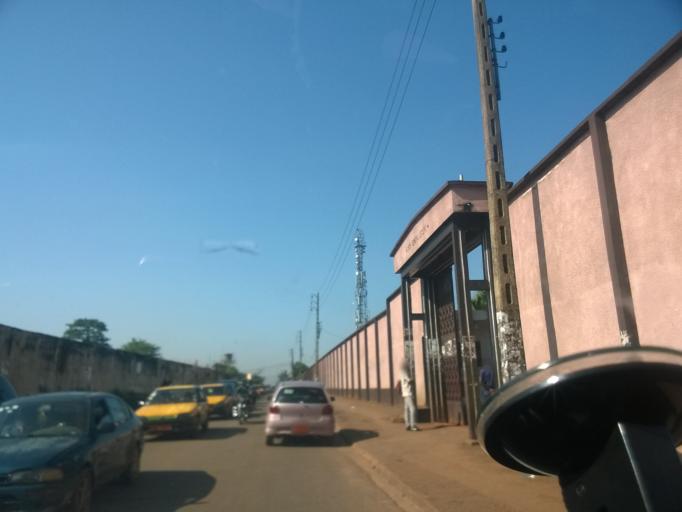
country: CM
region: Centre
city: Yaounde
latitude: 3.8560
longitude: 11.5089
